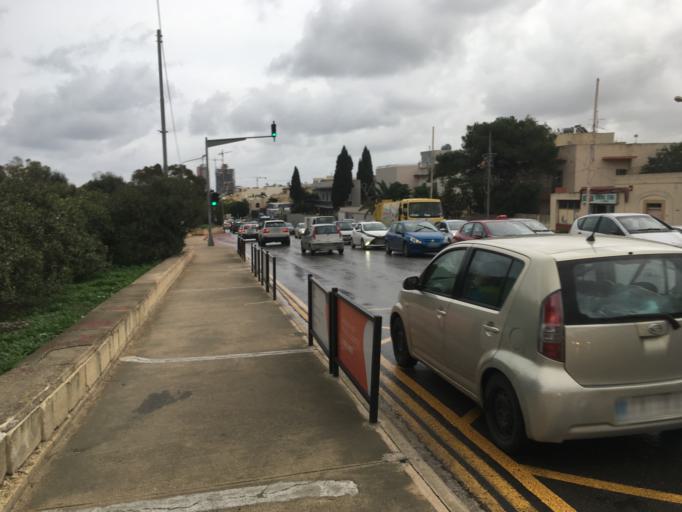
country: MT
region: Is-Swieqi
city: Swieqi
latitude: 35.9235
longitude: 14.4770
